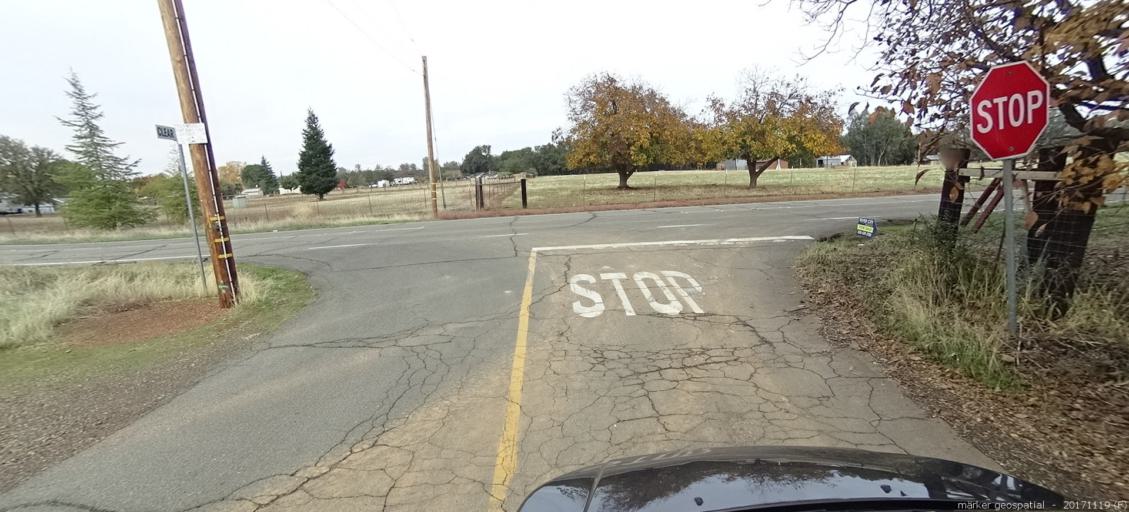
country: US
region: California
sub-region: Shasta County
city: Anderson
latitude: 40.4802
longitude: -122.2671
